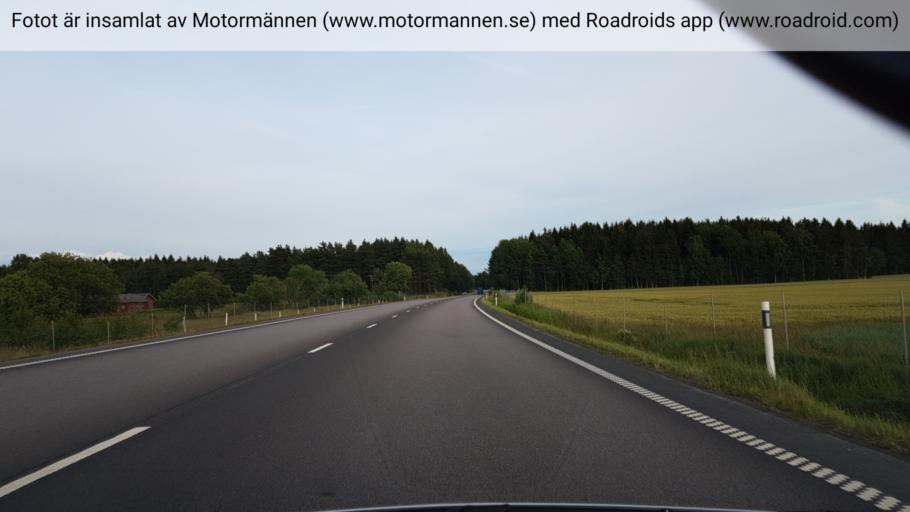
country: SE
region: Vaestra Goetaland
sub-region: Lidkopings Kommun
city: Vinninga
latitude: 58.4371
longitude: 13.2772
